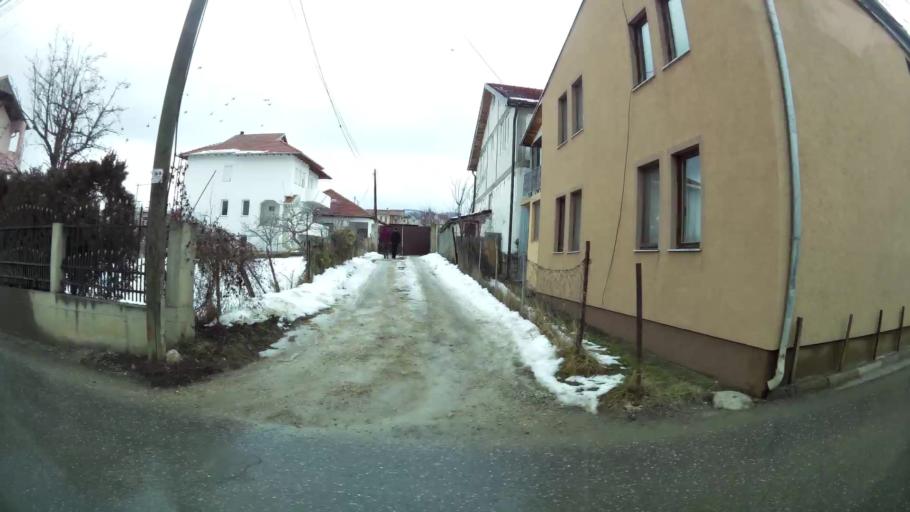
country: XK
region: Pristina
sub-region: Komuna e Prishtines
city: Pristina
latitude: 42.6456
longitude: 21.1869
